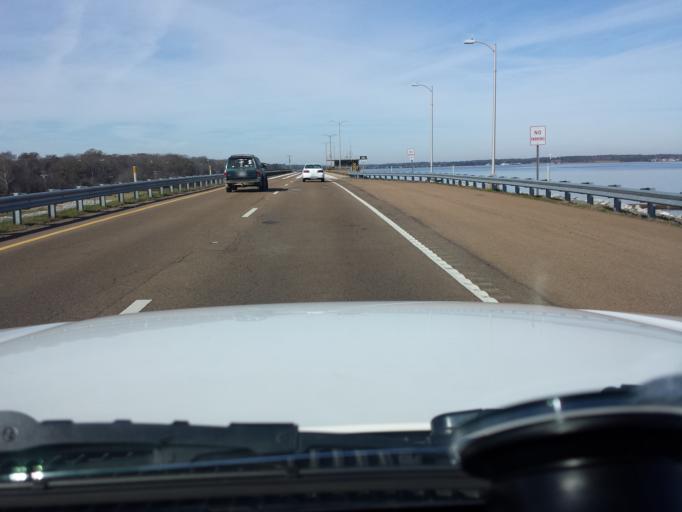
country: US
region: Mississippi
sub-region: Madison County
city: Ridgeland
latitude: 32.3963
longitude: -90.0628
